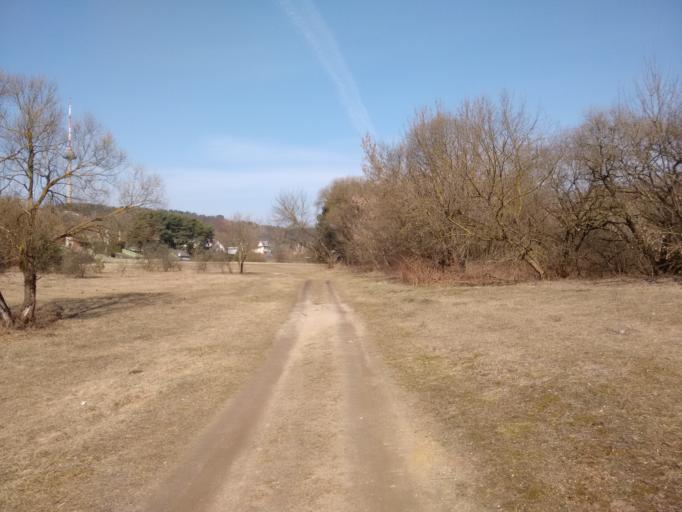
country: LT
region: Vilnius County
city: Vilkpede
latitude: 54.6776
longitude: 25.2306
